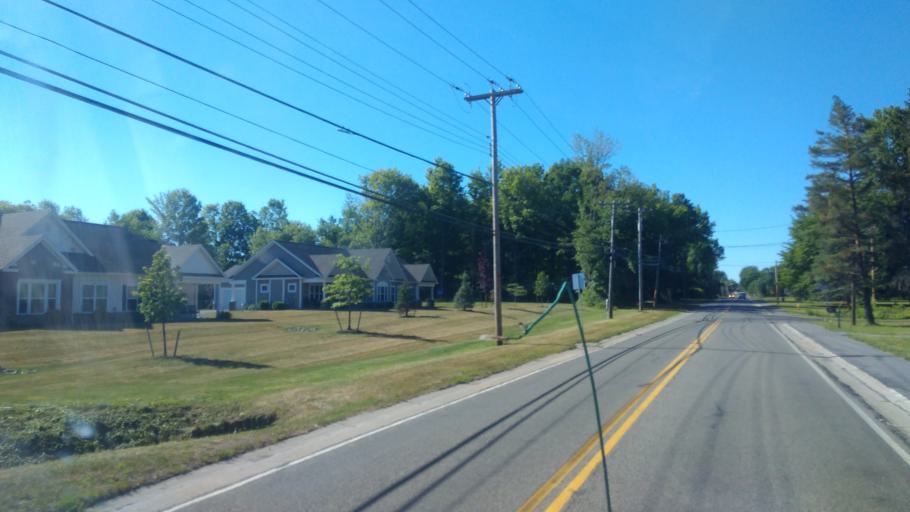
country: US
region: New York
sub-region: Monroe County
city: Webster
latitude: 43.2240
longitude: -77.4613
